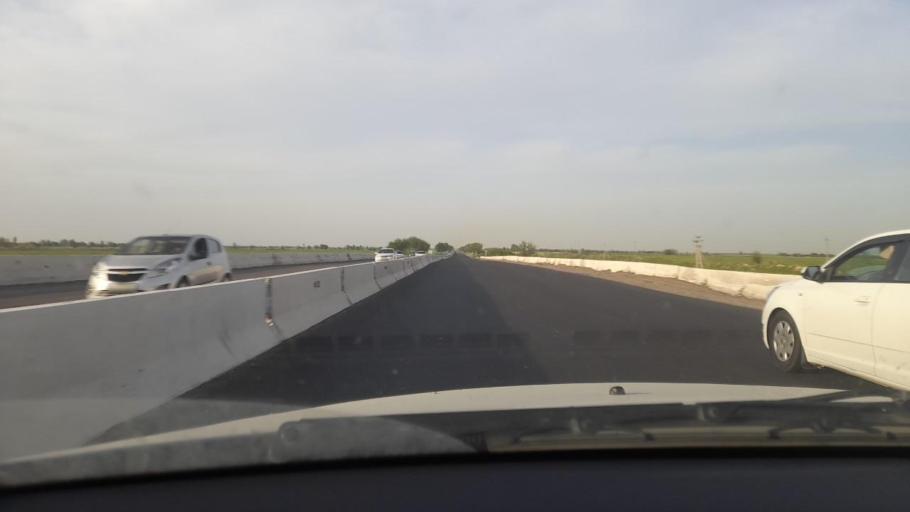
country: UZ
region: Jizzax
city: Gagarin
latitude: 40.5186
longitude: 68.3299
